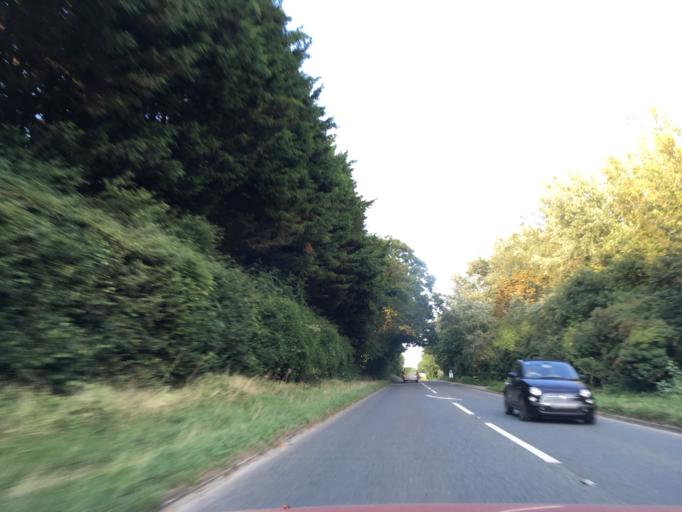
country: GB
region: England
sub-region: Gloucestershire
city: Bourton on the Water
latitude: 51.8890
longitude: -1.7660
